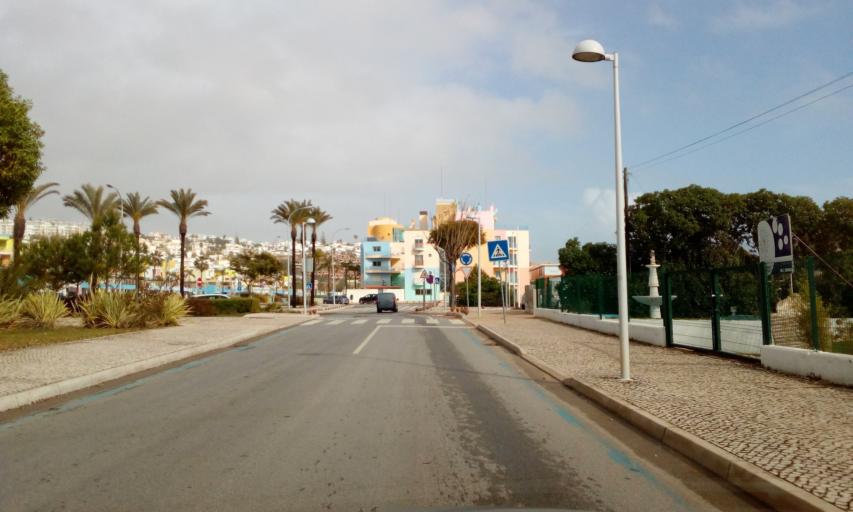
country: PT
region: Faro
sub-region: Albufeira
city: Albufeira
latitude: 37.0852
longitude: -8.2703
